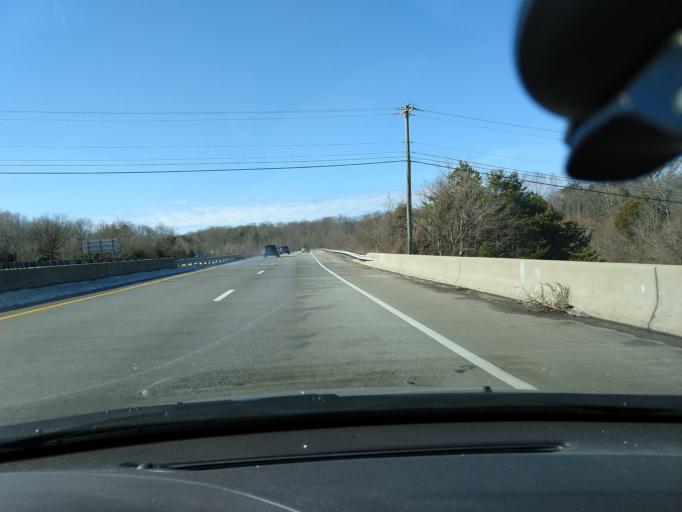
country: US
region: North Carolina
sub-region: Guilford County
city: Summerfield
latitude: 36.1166
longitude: -79.8918
